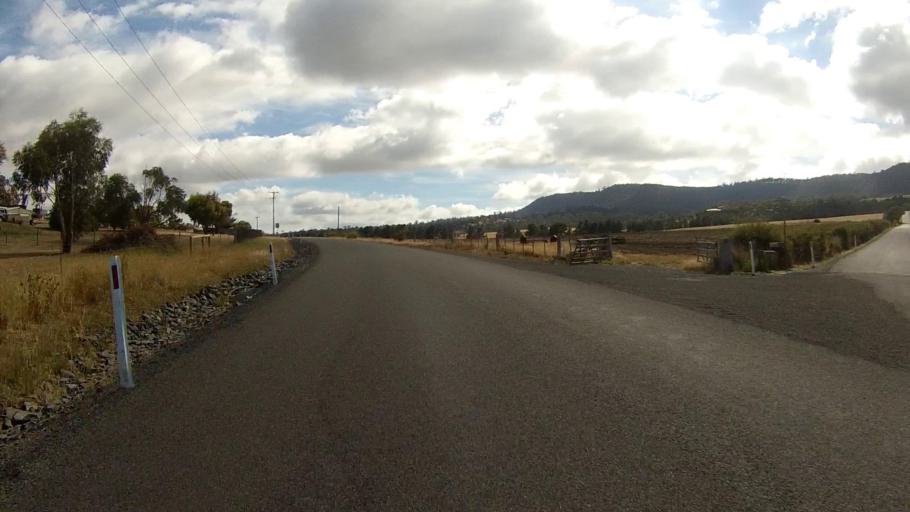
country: AU
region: Tasmania
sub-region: Brighton
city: Old Beach
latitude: -42.7664
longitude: 147.2991
